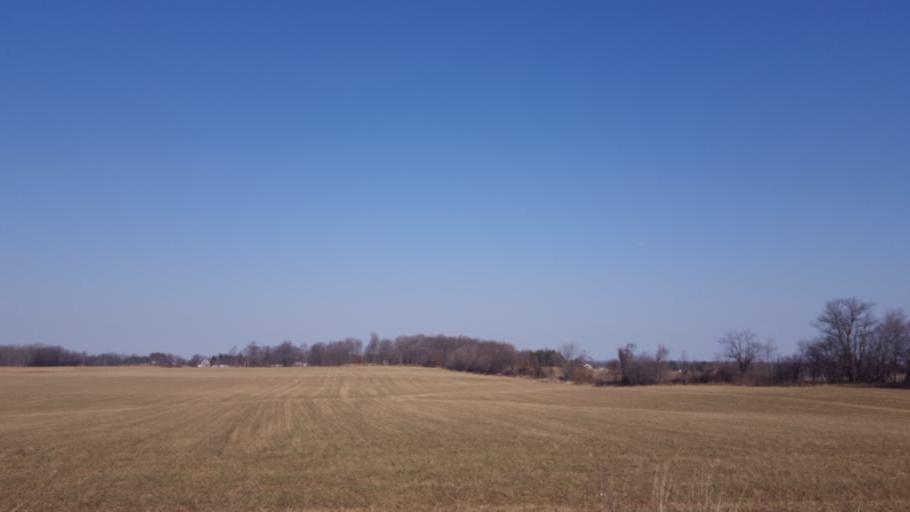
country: US
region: Ohio
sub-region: Richland County
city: Ontario
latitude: 40.8578
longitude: -82.5576
